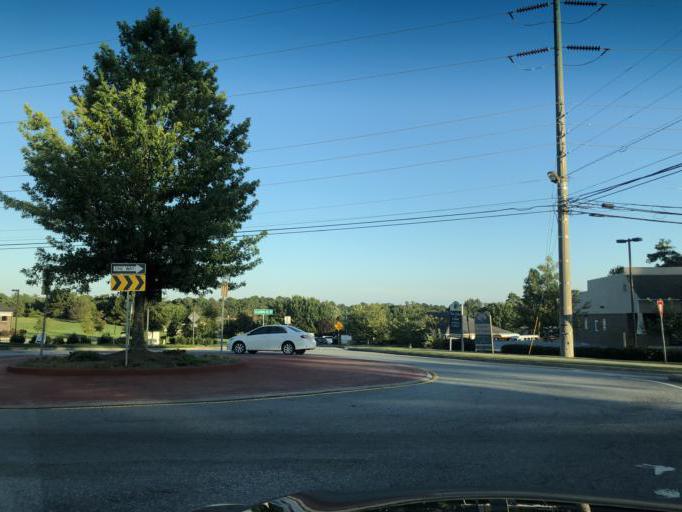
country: US
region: Georgia
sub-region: Muscogee County
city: Columbus
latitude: 32.5471
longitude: -84.8904
